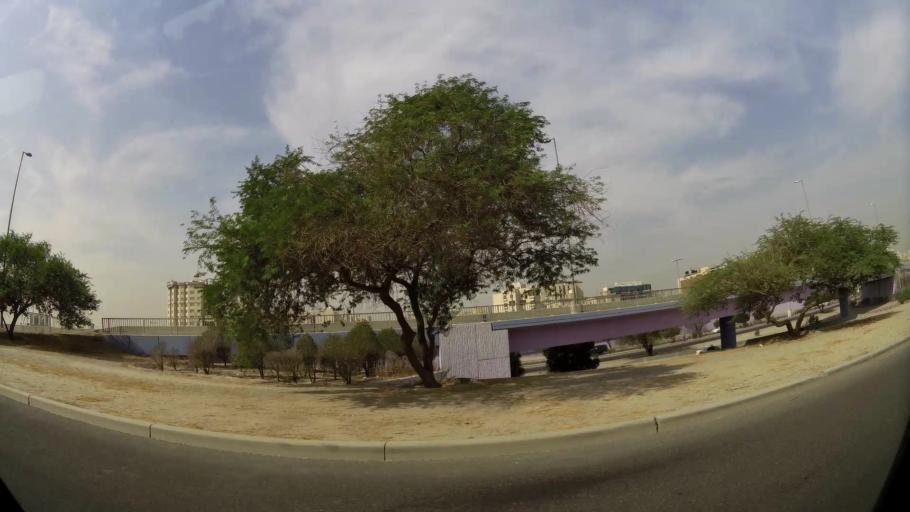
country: KW
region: Al Farwaniyah
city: Janub as Surrah
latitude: 29.2684
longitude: 47.9712
